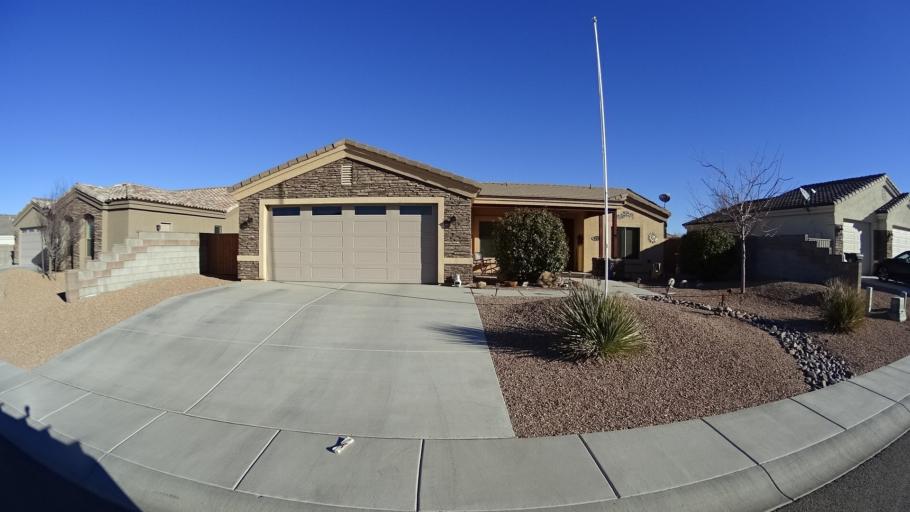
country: US
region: Arizona
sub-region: Mohave County
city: Kingman
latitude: 35.1937
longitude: -113.9968
